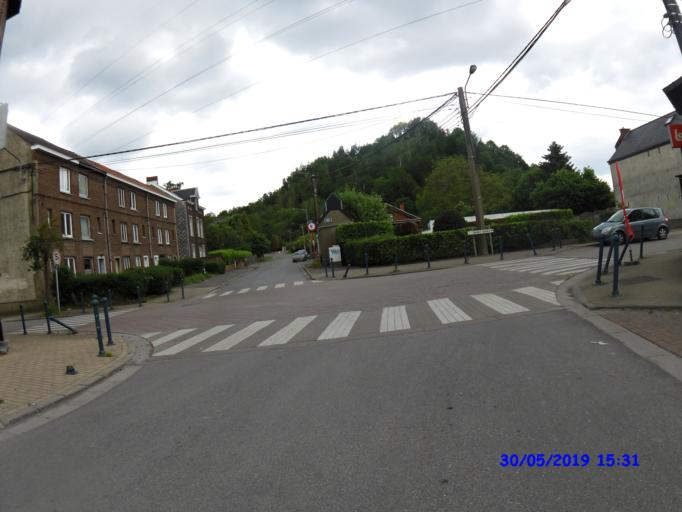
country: BE
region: Wallonia
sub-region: Province du Hainaut
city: Courcelles
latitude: 50.3999
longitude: 4.3729
